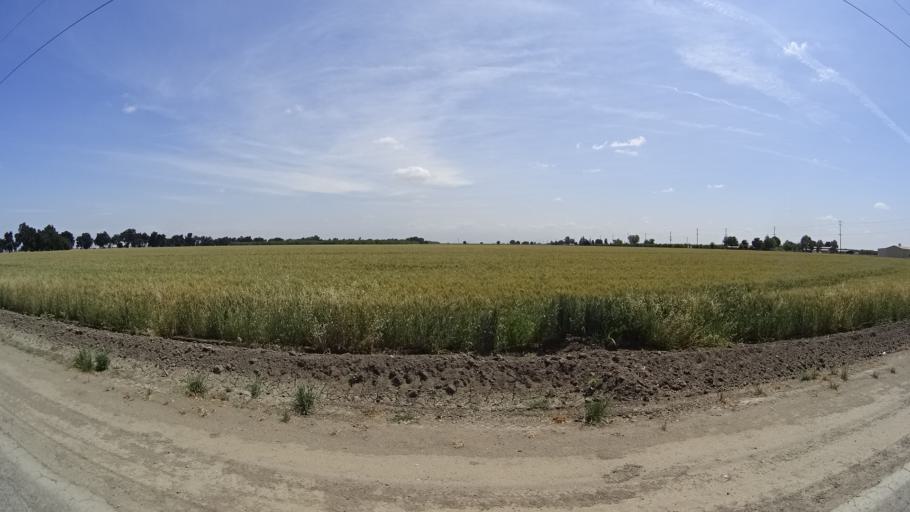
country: US
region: California
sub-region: Tulare County
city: Goshen
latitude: 36.2851
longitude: -119.4745
